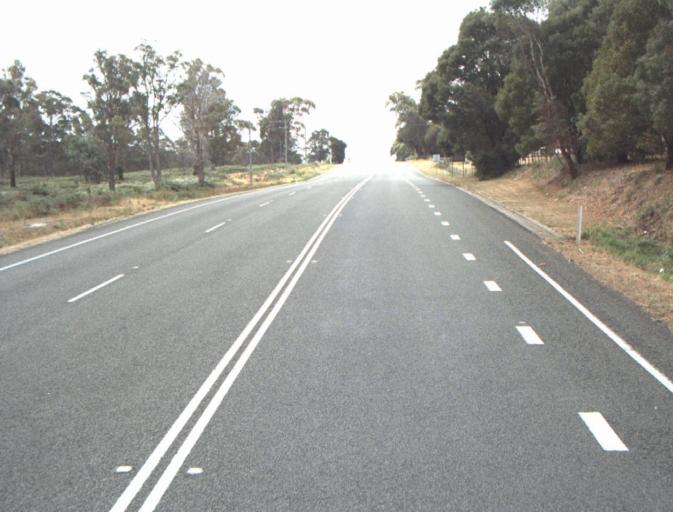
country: AU
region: Tasmania
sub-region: Launceston
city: Mayfield
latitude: -41.2806
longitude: 147.0385
